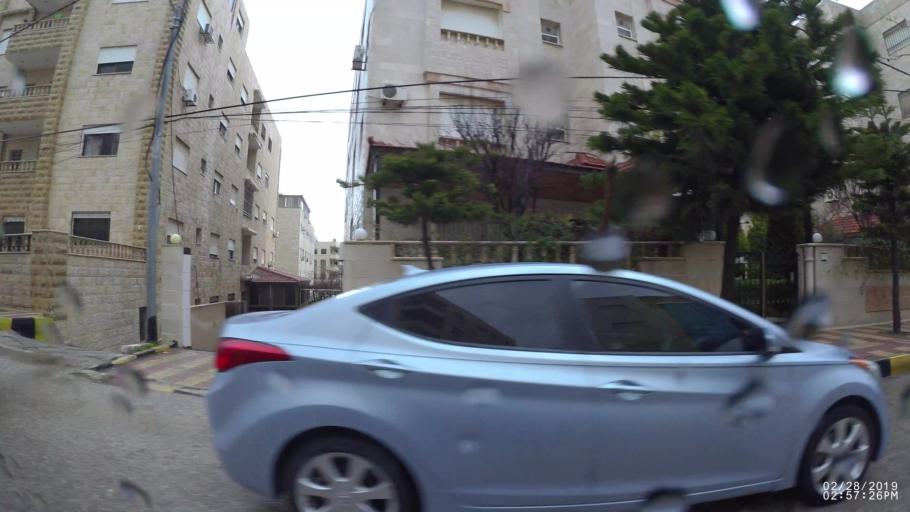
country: JO
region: Amman
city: Al Jubayhah
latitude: 32.0263
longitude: 35.8706
